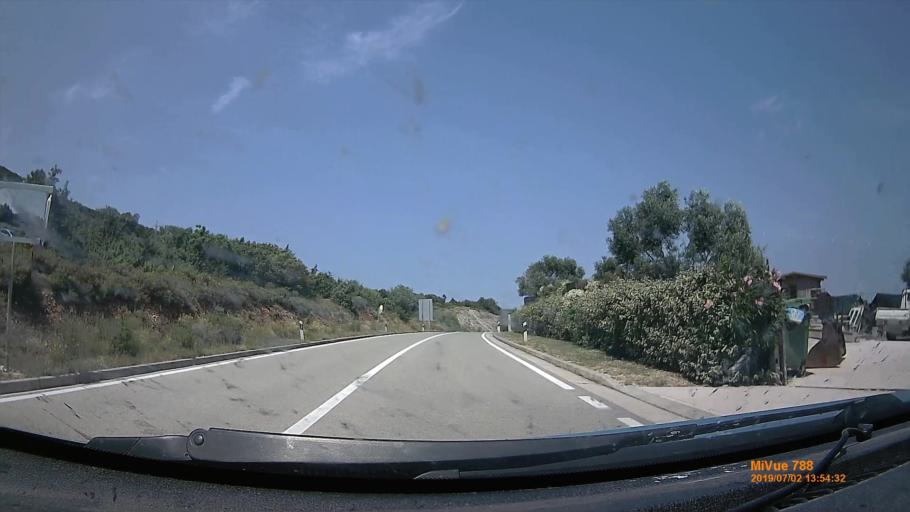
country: HR
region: Primorsko-Goranska
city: Mali Losinj
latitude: 44.6399
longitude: 14.3907
